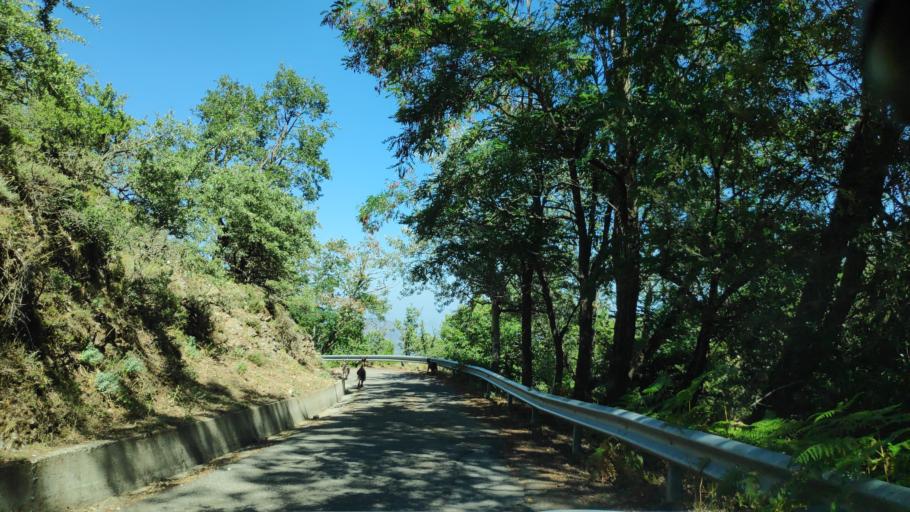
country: IT
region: Calabria
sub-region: Provincia di Reggio Calabria
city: Africo Vecchio
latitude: 38.0395
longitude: 15.9502
